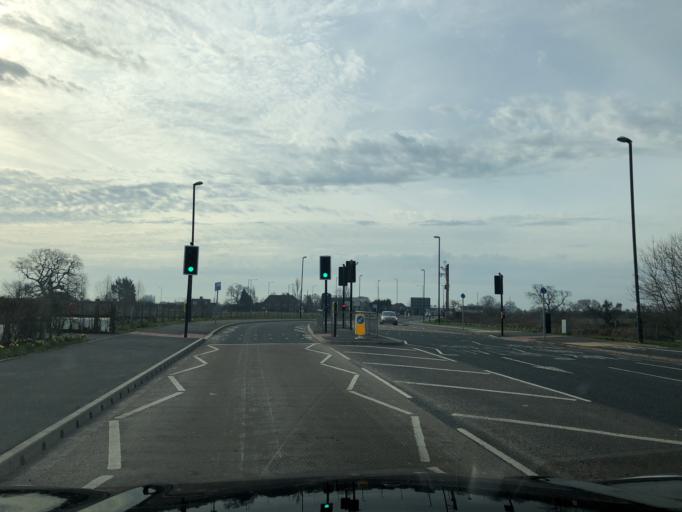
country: GB
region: England
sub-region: City of York
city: Huntington
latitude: 53.9819
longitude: -1.0502
